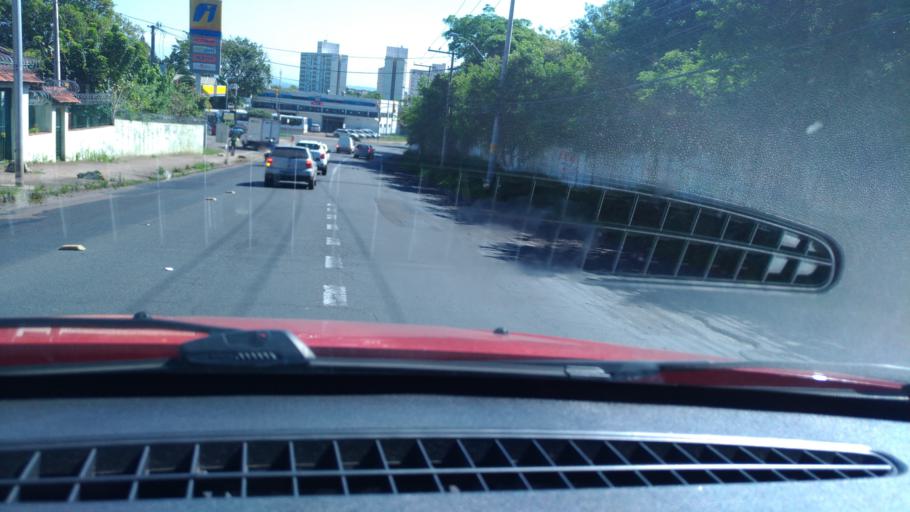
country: BR
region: Rio Grande do Sul
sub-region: Cachoeirinha
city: Cachoeirinha
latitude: -30.0327
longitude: -51.1350
